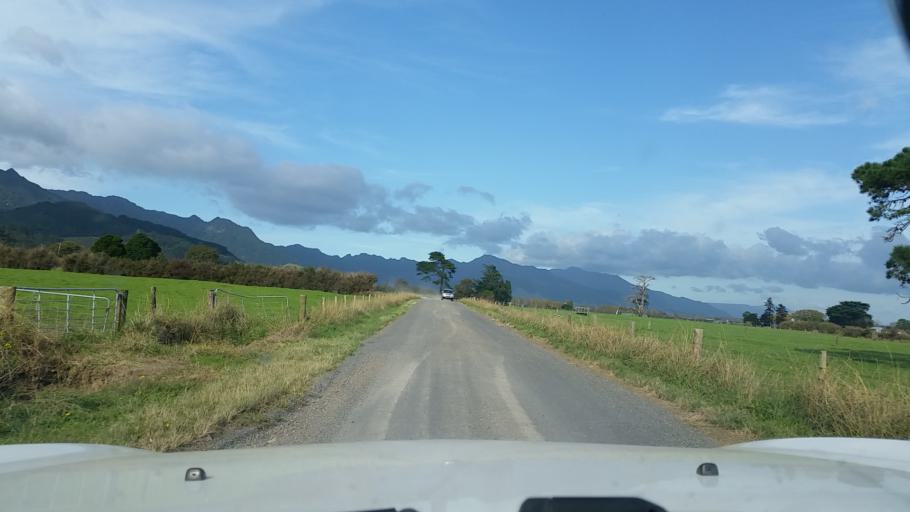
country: NZ
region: Bay of Plenty
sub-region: Western Bay of Plenty District
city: Katikati
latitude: -37.5615
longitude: 175.7460
